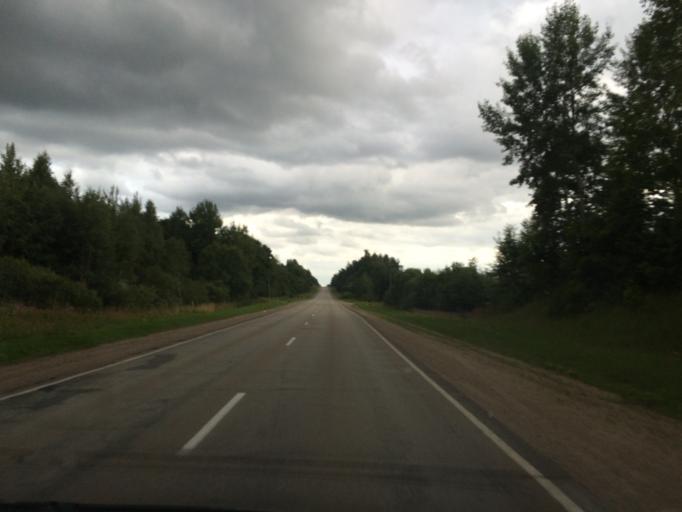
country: LV
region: Rezekne
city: Rezekne
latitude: 56.5676
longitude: 27.3682
